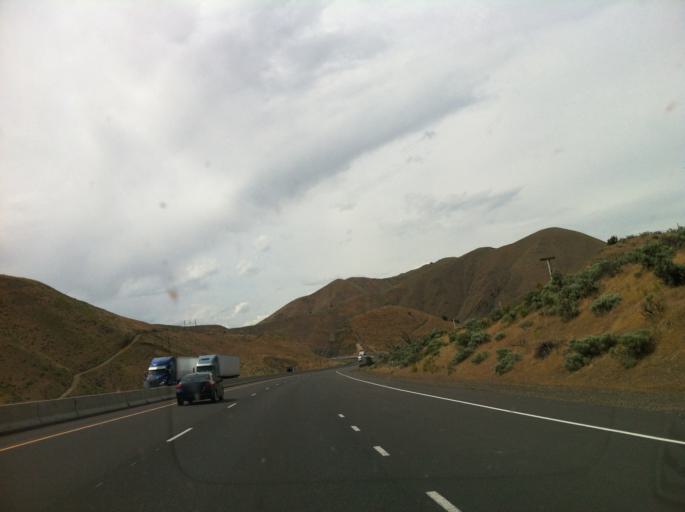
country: US
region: Idaho
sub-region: Washington County
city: Weiser
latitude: 44.4329
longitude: -117.3194
